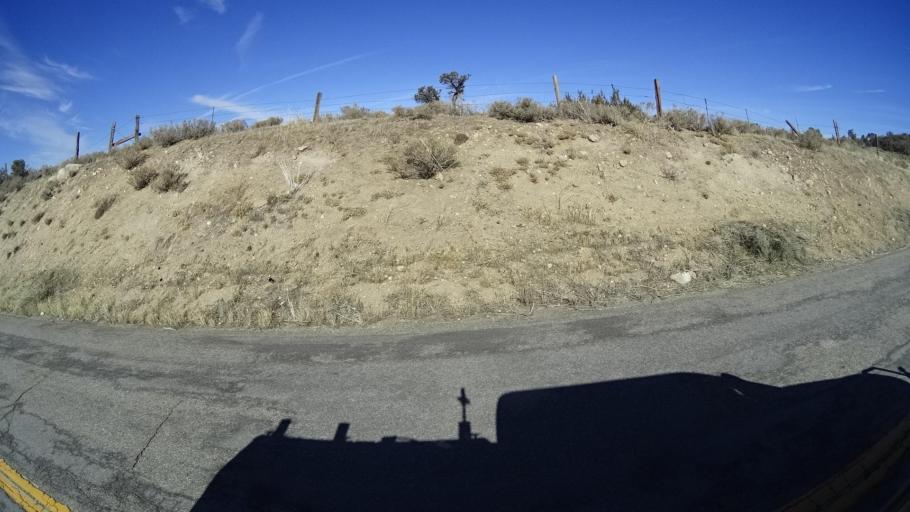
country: US
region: California
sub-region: Kern County
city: Pine Mountain Club
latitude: 34.8688
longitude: -119.3243
